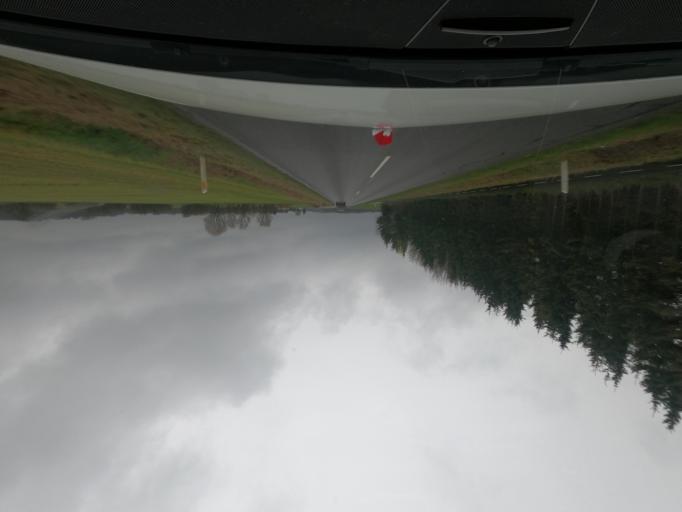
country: DK
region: South Denmark
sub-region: Haderslev Kommune
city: Starup
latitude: 55.2086
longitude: 9.5136
